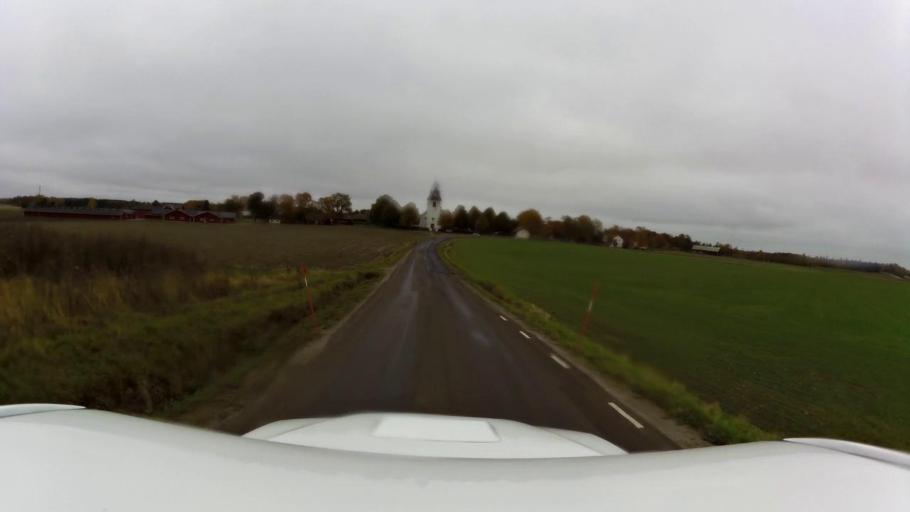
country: SE
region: OEstergoetland
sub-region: Linkopings Kommun
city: Ekangen
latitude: 58.4506
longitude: 15.7070
